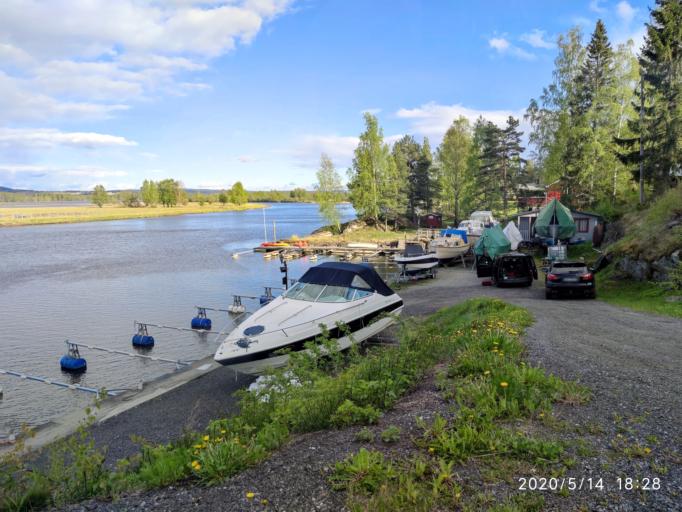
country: NO
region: Akershus
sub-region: Fet
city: Fetsund
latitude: 59.8984
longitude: 11.1117
